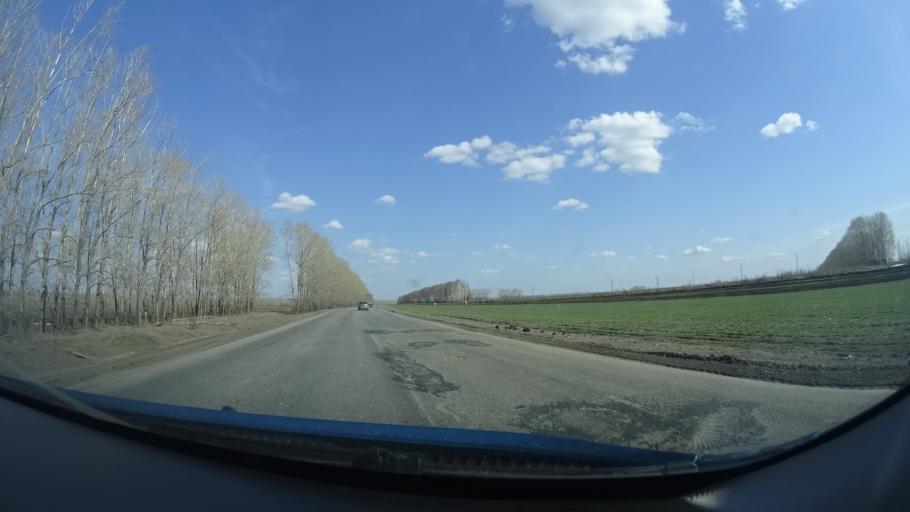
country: RU
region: Bashkortostan
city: Buzdyak
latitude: 54.6220
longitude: 54.4087
